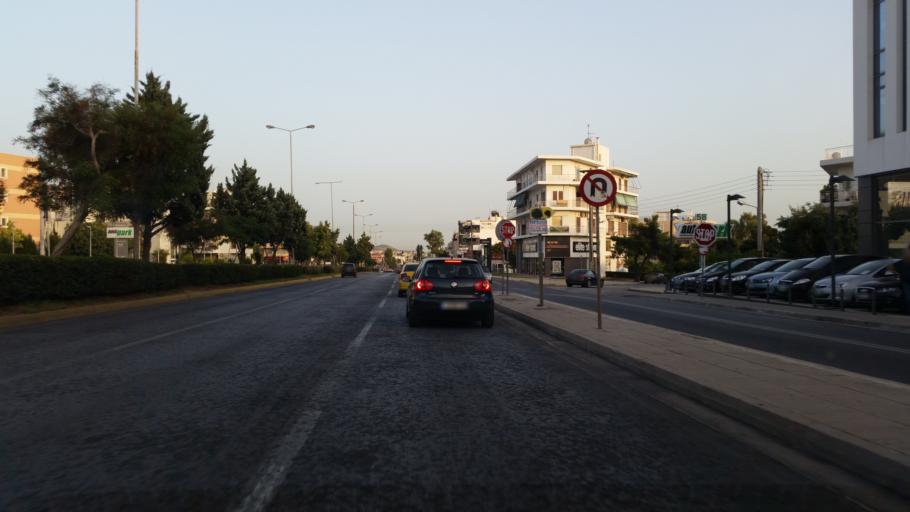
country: GR
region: Attica
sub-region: Nomarchia Athinas
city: Glyfada
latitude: 37.8792
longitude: 23.7544
